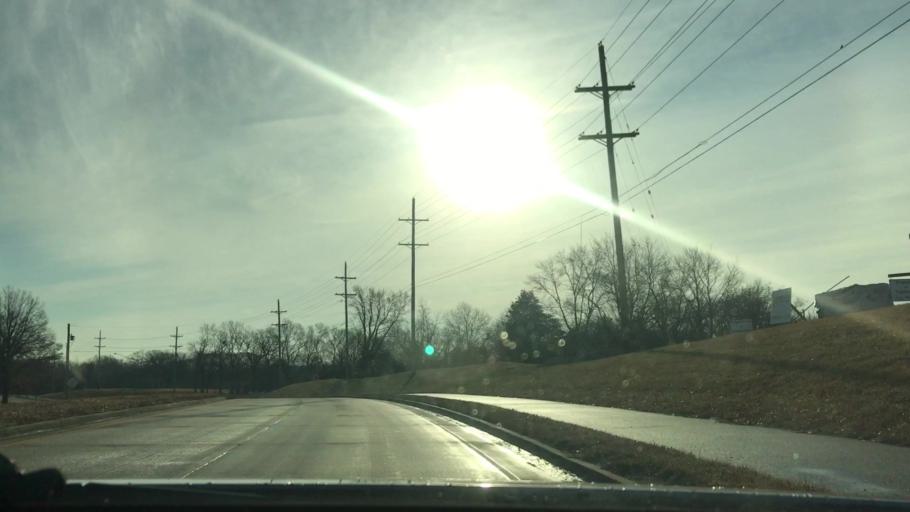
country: US
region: Missouri
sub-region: Platte County
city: Weatherby Lake
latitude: 39.2127
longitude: -94.7264
